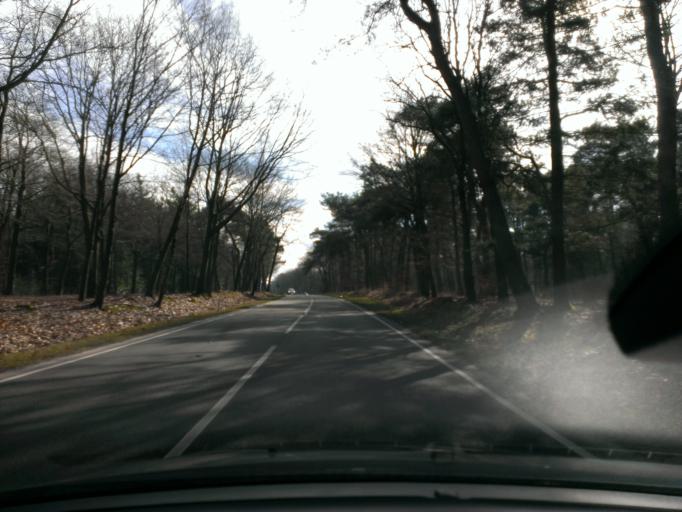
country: NL
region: Gelderland
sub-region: Gemeente Heerde
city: Heerde
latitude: 52.4181
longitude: 6.0131
